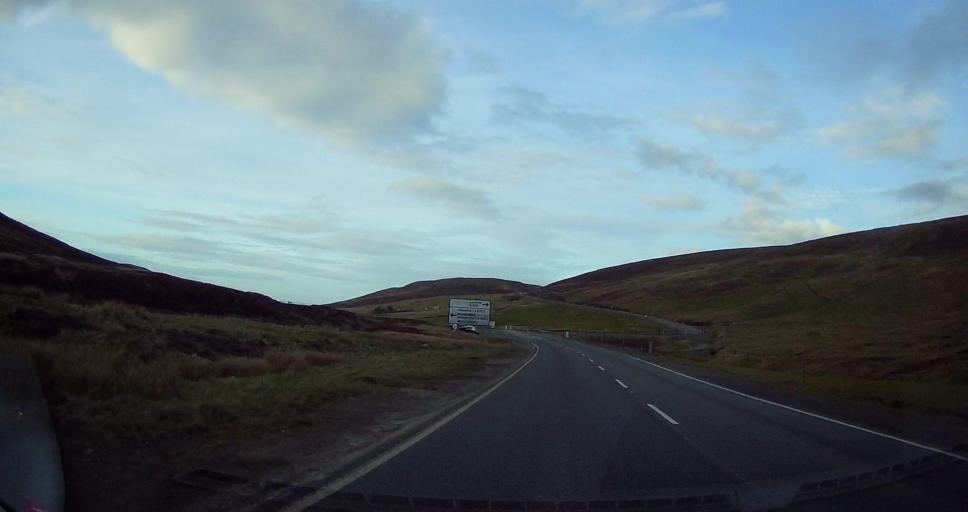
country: GB
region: Scotland
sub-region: Shetland Islands
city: Lerwick
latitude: 60.1596
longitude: -1.2290
